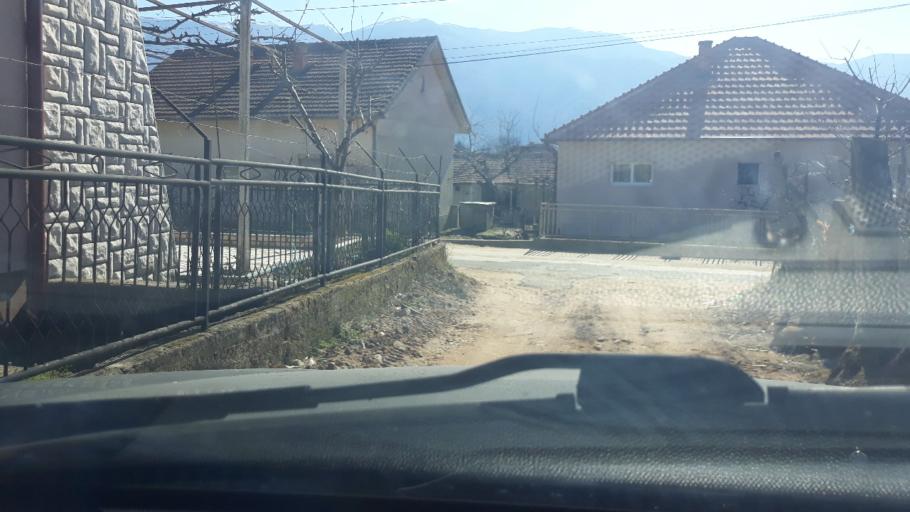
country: MK
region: Novo Selo
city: Novo Selo
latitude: 41.4163
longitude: 22.8799
